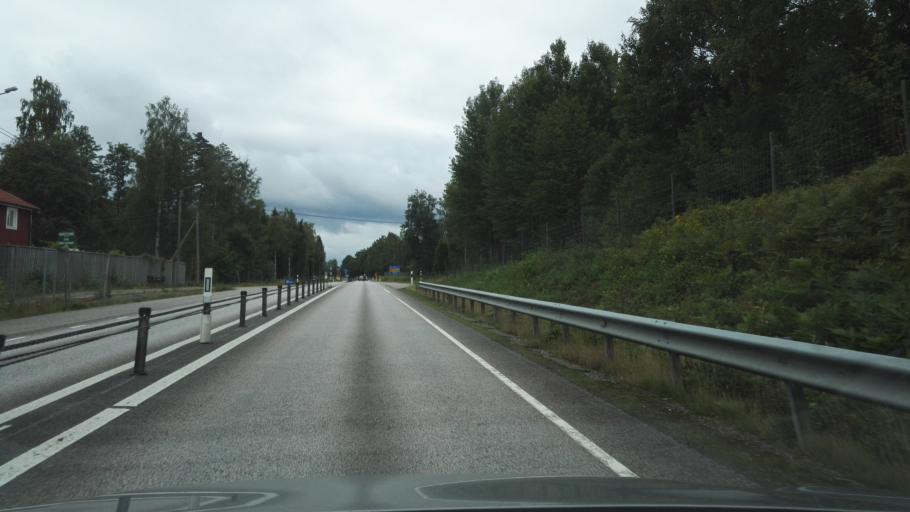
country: SE
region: Kronoberg
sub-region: Vaxjo Kommun
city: Braas
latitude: 56.9884
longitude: 14.9933
